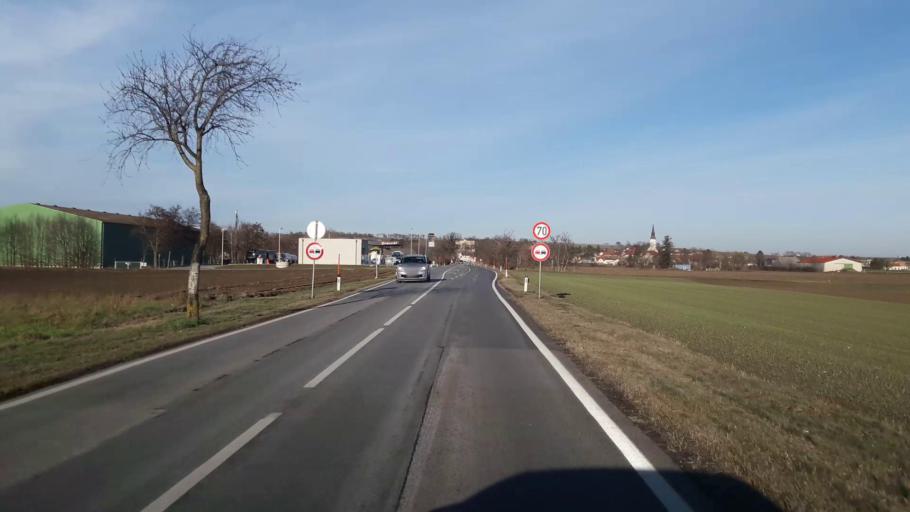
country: AT
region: Lower Austria
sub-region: Politischer Bezirk Mistelbach
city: Bockfliess
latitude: 48.3528
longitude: 16.5994
